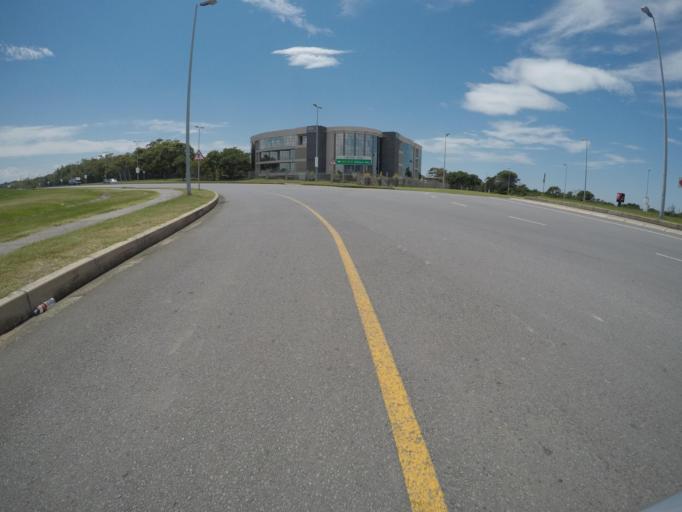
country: ZA
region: Eastern Cape
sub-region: Buffalo City Metropolitan Municipality
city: East London
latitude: -33.0491
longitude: 27.8529
